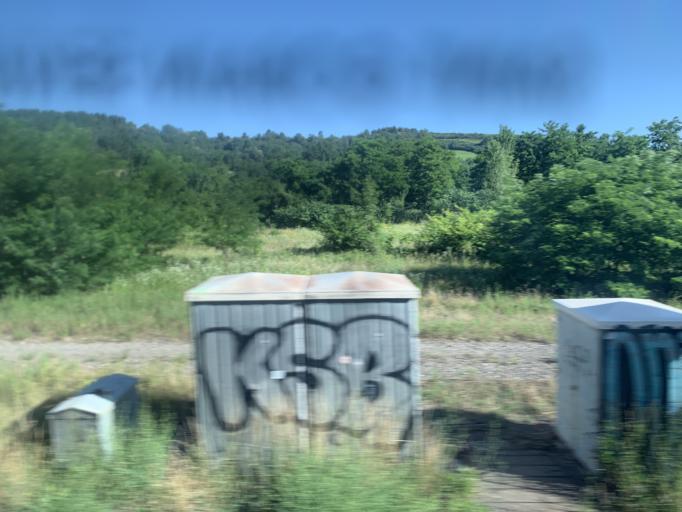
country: FR
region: Rhone-Alpes
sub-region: Departement de la Loire
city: Saint-Jean-Bonnefonds
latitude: 45.4397
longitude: 4.4605
